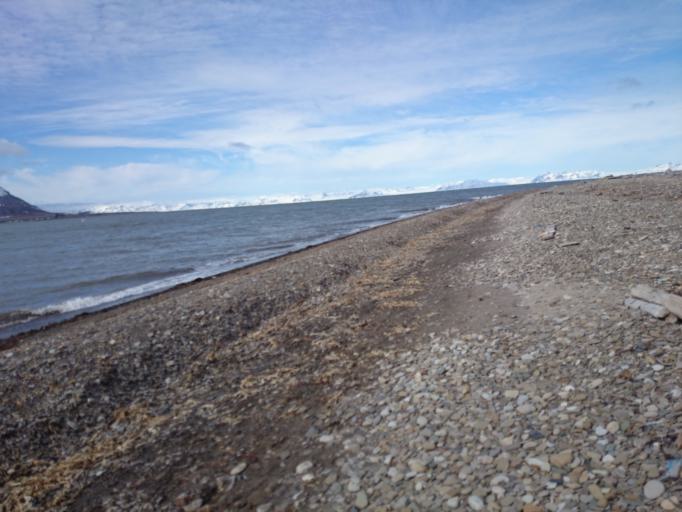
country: SJ
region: Svalbard
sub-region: Spitsbergen
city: Longyearbyen
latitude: 78.2503
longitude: 15.6782
